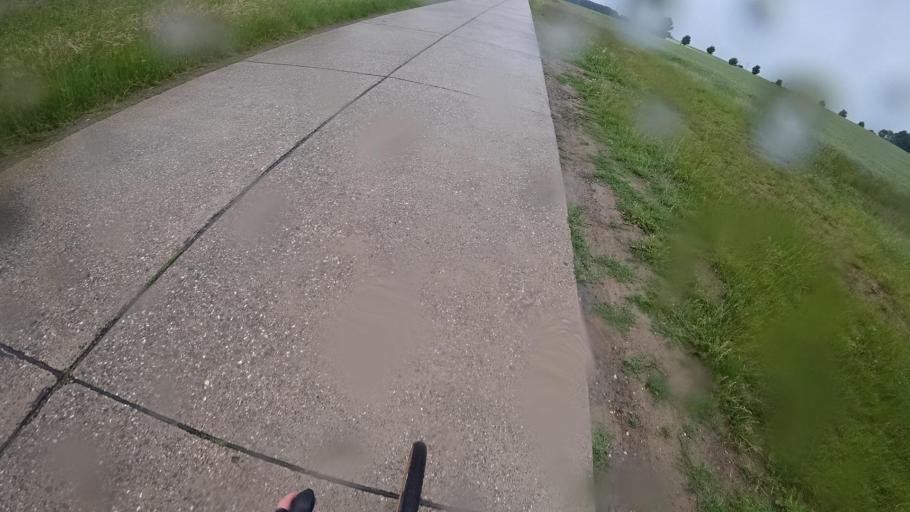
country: DE
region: Rheinland-Pfalz
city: Dernau
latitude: 50.5521
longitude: 7.0426
